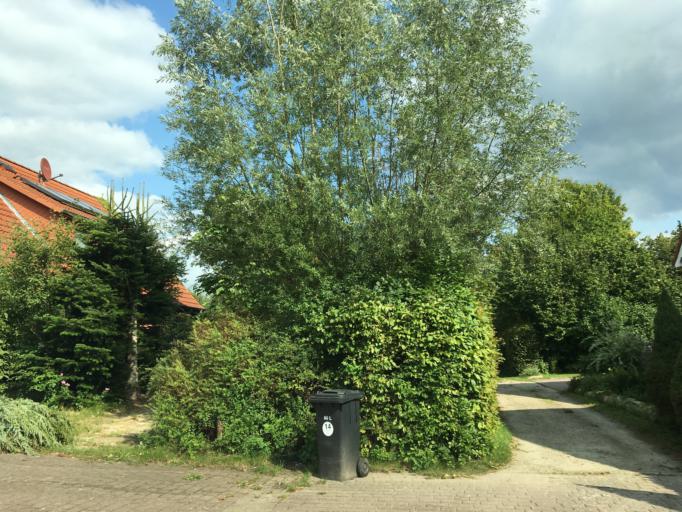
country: DE
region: Lower Saxony
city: Melbeck
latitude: 53.2068
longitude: 10.3917
